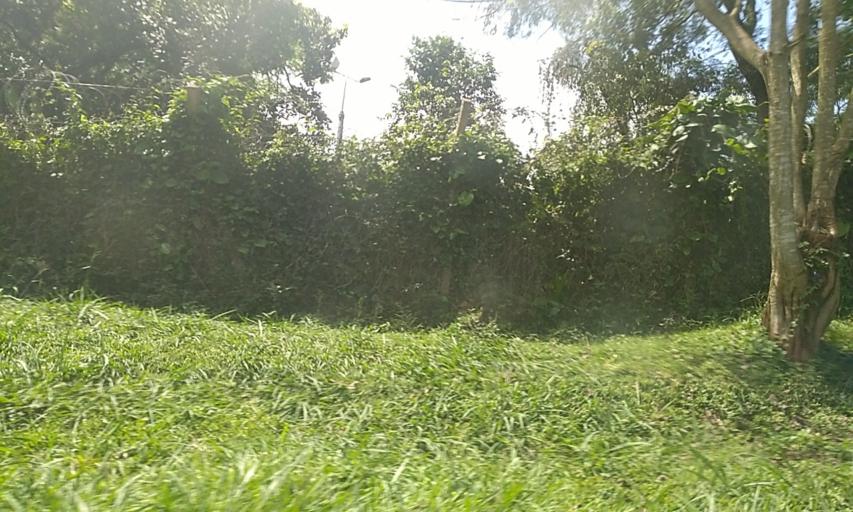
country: UG
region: Central Region
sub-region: Kampala District
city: Kampala
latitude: 0.3362
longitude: 32.5985
